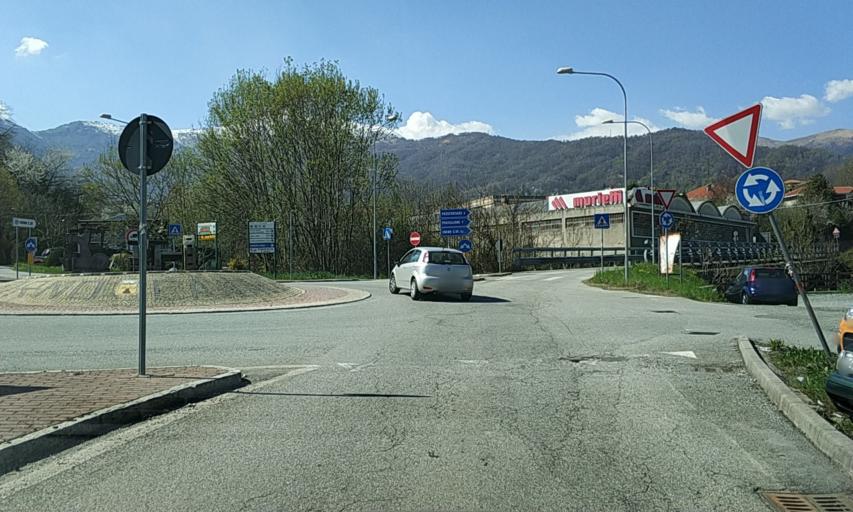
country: IT
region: Piedmont
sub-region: Provincia di Torino
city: Forno Canavese
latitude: 45.3392
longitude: 7.5969
